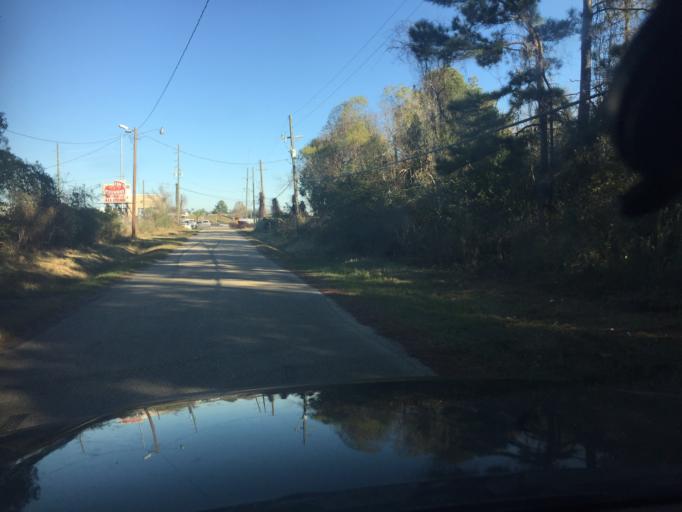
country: US
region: Louisiana
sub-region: Saint Tammany Parish
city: Slidell
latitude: 30.2436
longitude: -89.7635
